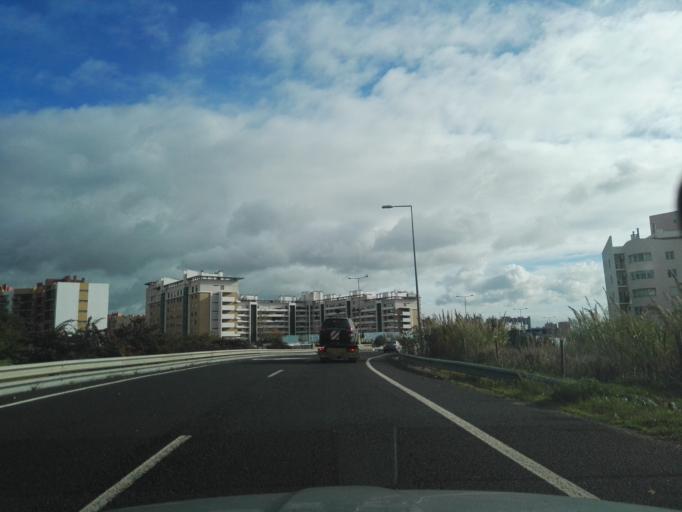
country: PT
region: Lisbon
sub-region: Odivelas
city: Pontinha
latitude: 38.7564
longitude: -9.1729
